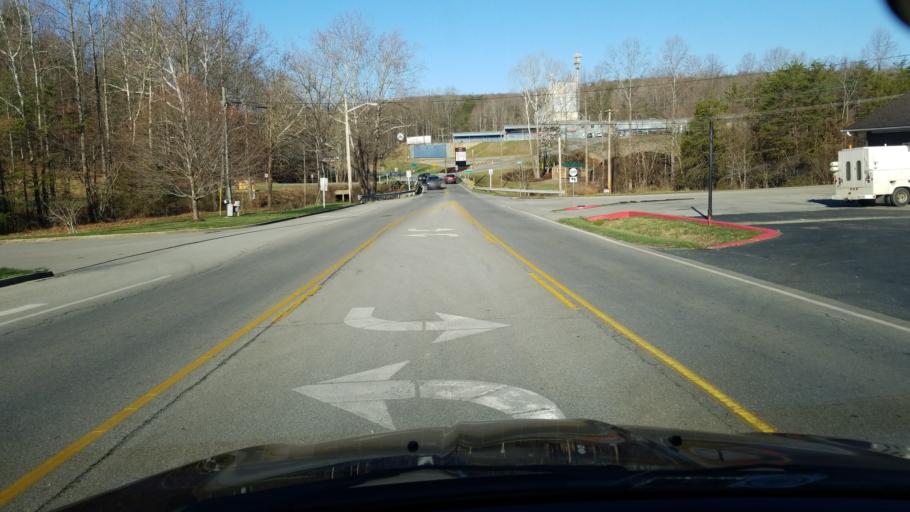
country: US
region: Virginia
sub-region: Franklin County
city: Rocky Mount
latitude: 36.9907
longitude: -79.9029
